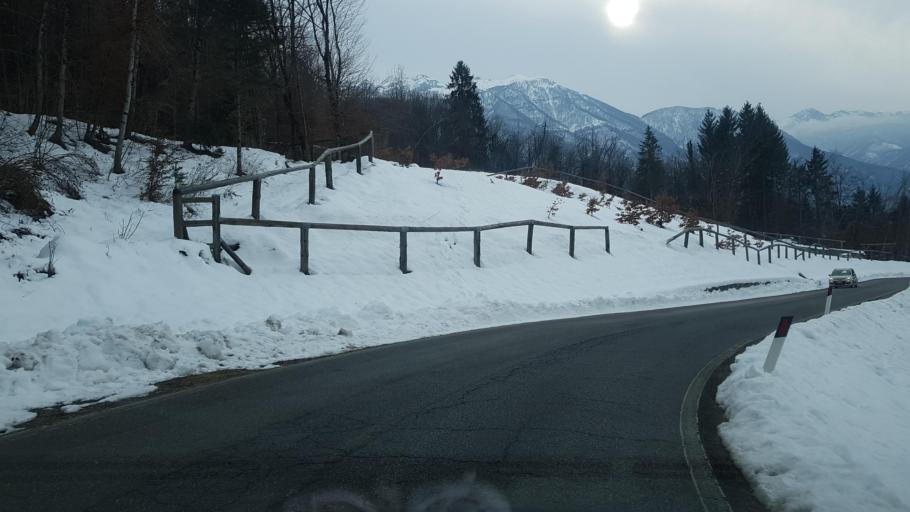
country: IT
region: Friuli Venezia Giulia
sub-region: Provincia di Udine
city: Villa Santina
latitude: 46.4220
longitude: 12.9220
